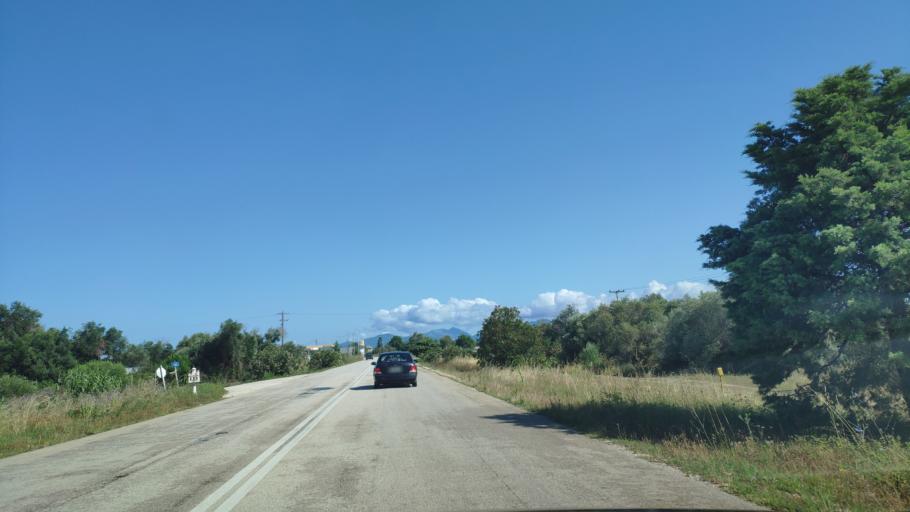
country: GR
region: Epirus
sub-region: Nomos Prevezis
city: Preveza
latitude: 38.9787
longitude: 20.7178
